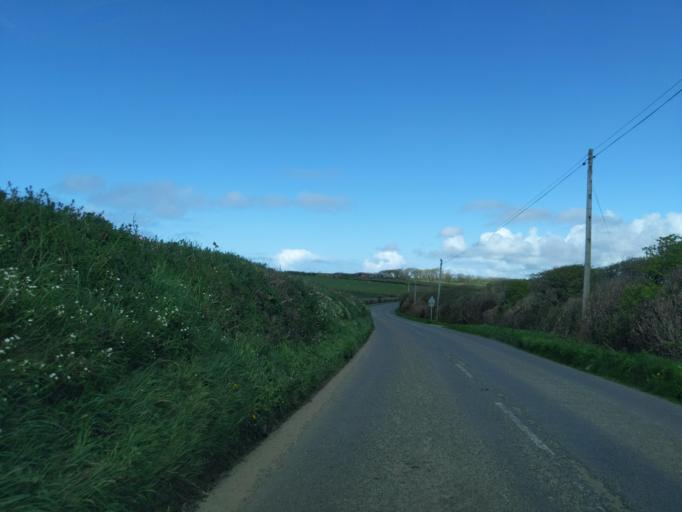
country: GB
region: England
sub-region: Cornwall
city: Tintagel
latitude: 50.5884
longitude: -4.7803
